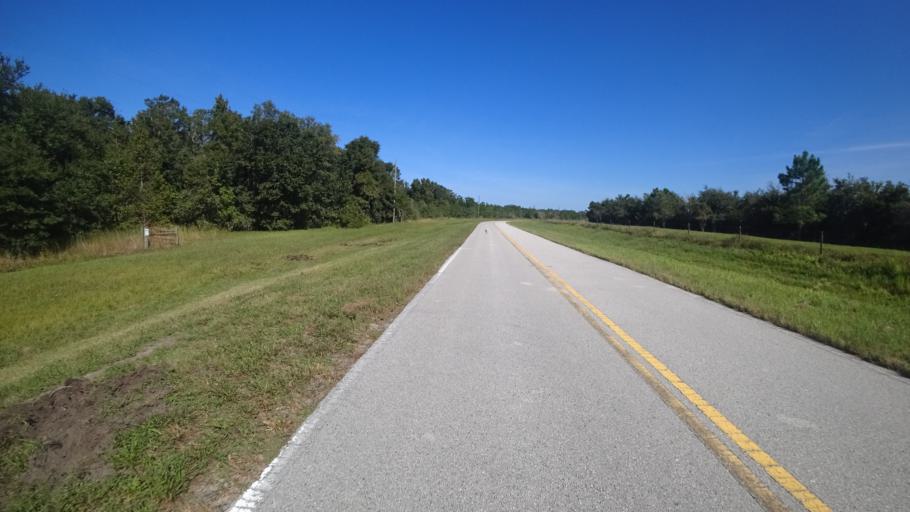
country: US
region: Florida
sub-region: Hillsborough County
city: Wimauma
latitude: 27.5853
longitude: -82.1819
